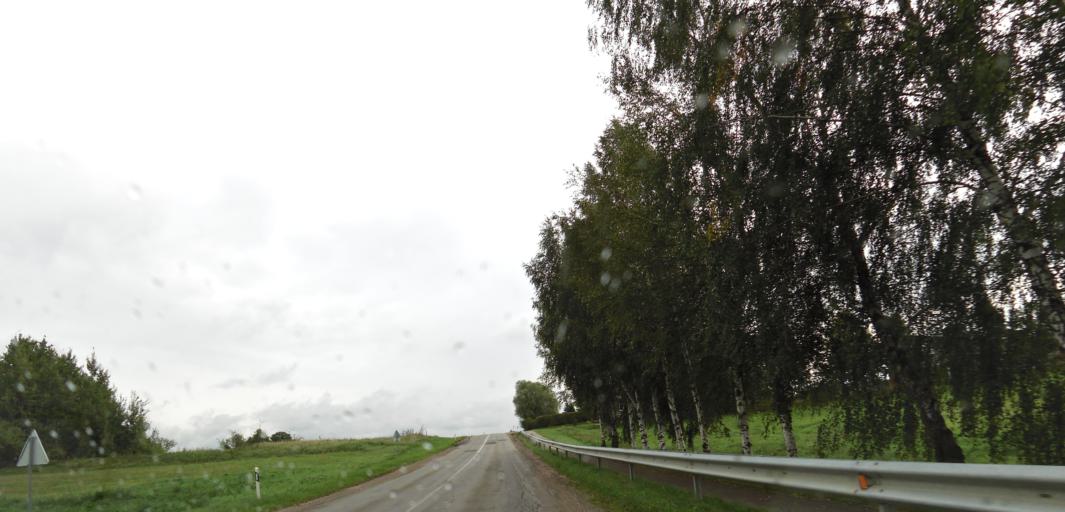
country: LT
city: Moletai
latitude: 55.2320
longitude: 25.3932
